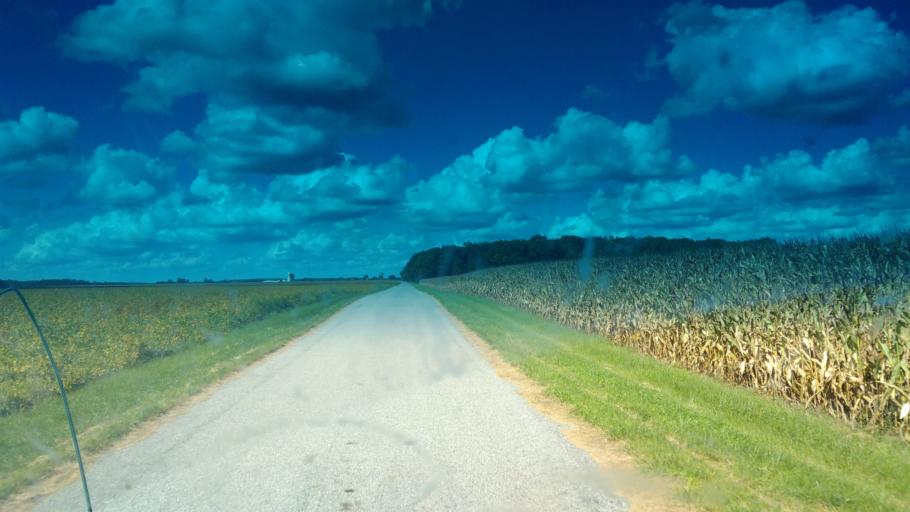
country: US
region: Ohio
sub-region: Hardin County
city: Kenton
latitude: 40.5034
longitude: -83.5384
